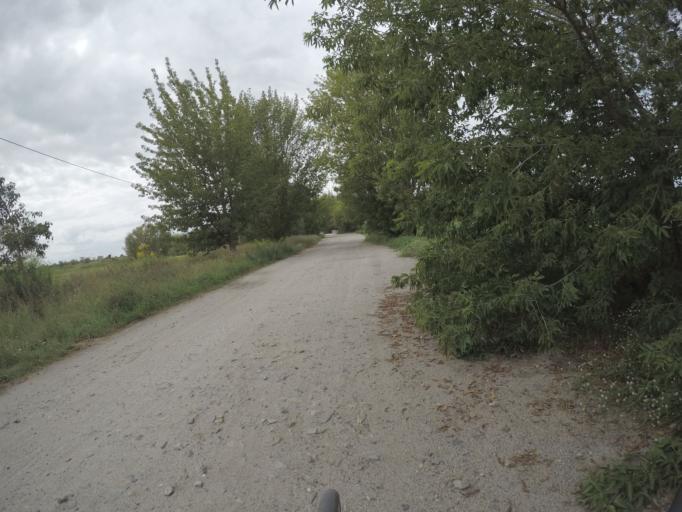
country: DE
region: Brandenburg
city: Nauen
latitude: 52.6129
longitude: 12.9224
